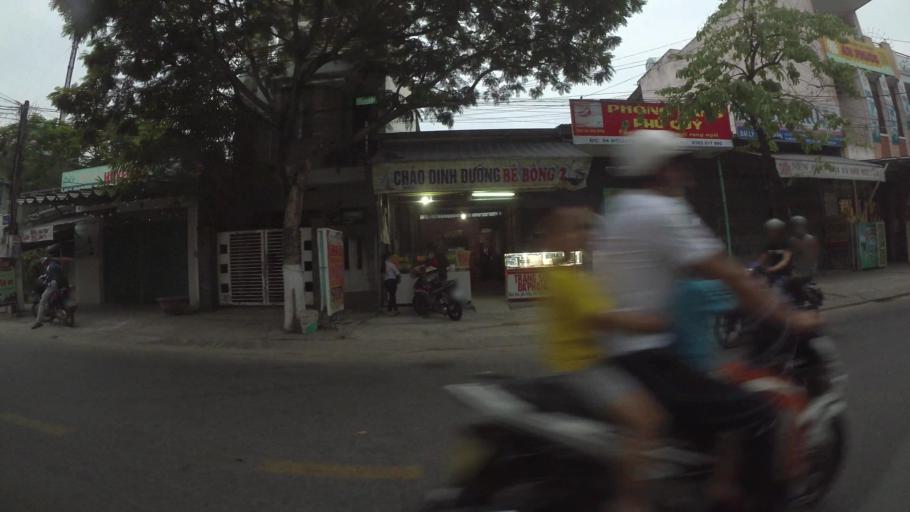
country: VN
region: Da Nang
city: Thanh Khe
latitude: 16.0503
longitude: 108.1779
